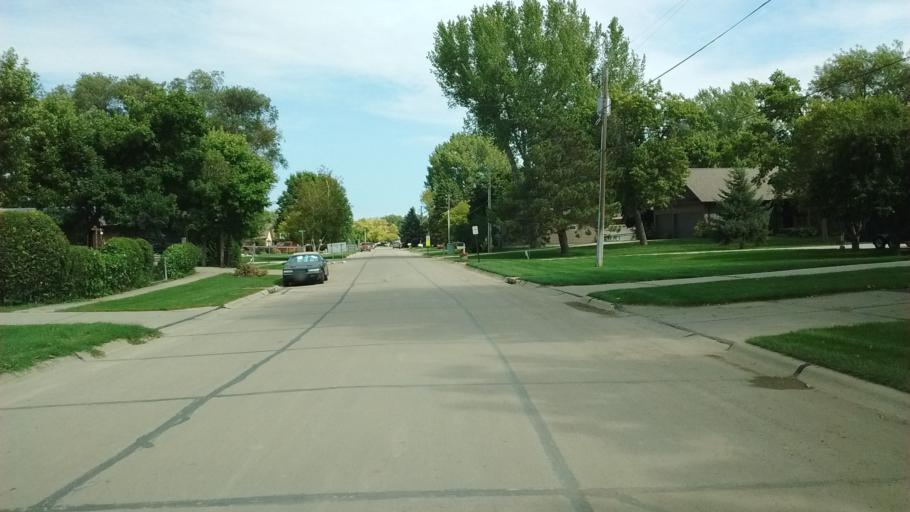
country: US
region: South Dakota
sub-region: Union County
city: North Sioux City
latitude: 42.5421
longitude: -96.5252
